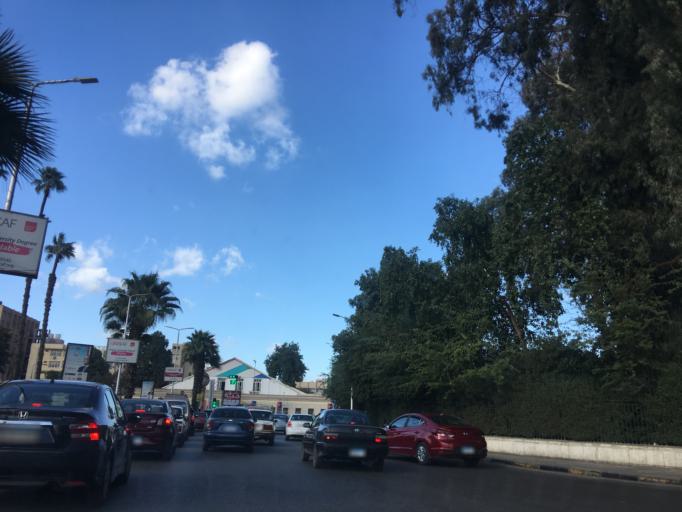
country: EG
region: Al Jizah
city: Al Jizah
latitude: 30.0288
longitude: 31.2105
